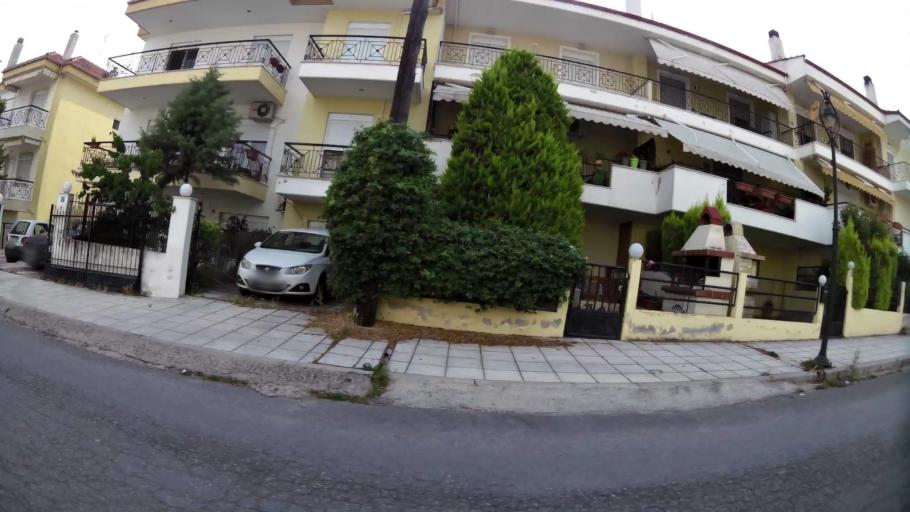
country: GR
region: Central Macedonia
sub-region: Nomos Thessalonikis
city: Oraiokastro
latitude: 40.7199
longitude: 22.9103
